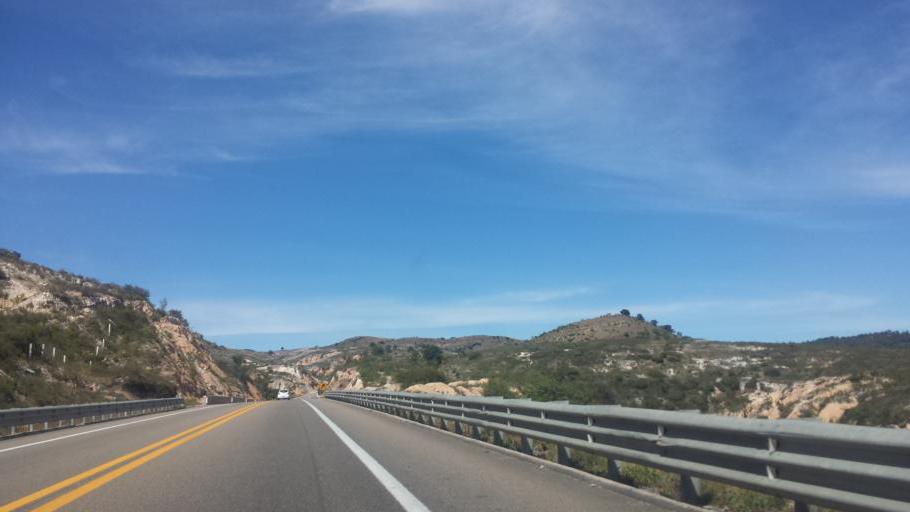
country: MX
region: Oaxaca
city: San Andres Sinaxtla
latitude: 17.5894
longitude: -97.3166
